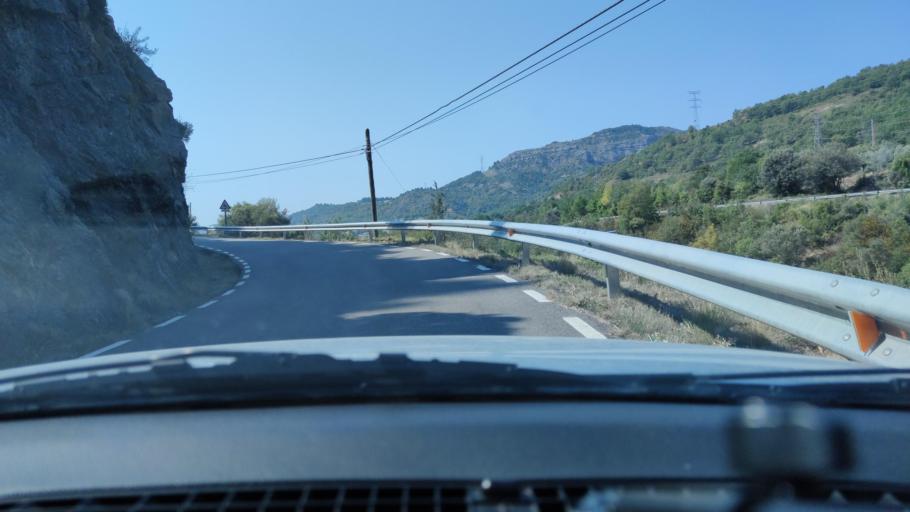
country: ES
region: Catalonia
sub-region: Provincia de Lleida
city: Senterada
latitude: 42.2859
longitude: 0.9374
